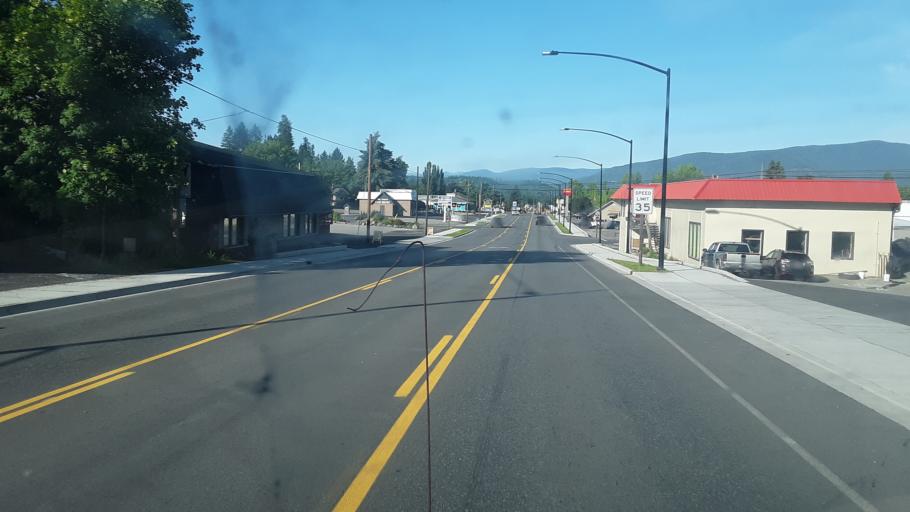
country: US
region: Idaho
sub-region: Boundary County
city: Bonners Ferry
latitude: 48.6869
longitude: -116.3171
